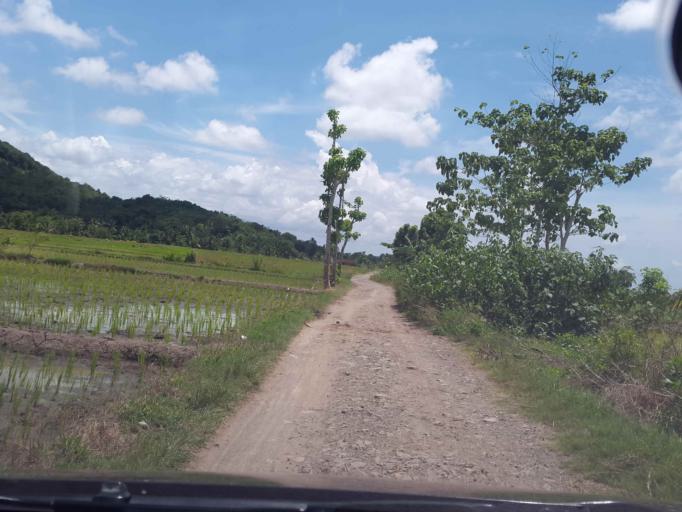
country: ID
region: West Nusa Tenggara
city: Ranggagata
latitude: -8.7200
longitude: 116.1671
